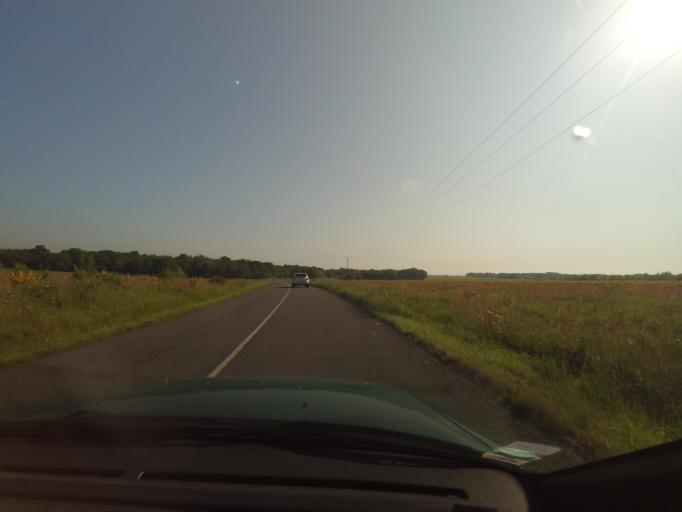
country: FR
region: Pays de la Loire
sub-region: Departement de la Loire-Atlantique
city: Maisdon-sur-Sevre
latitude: 47.1114
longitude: -1.3716
